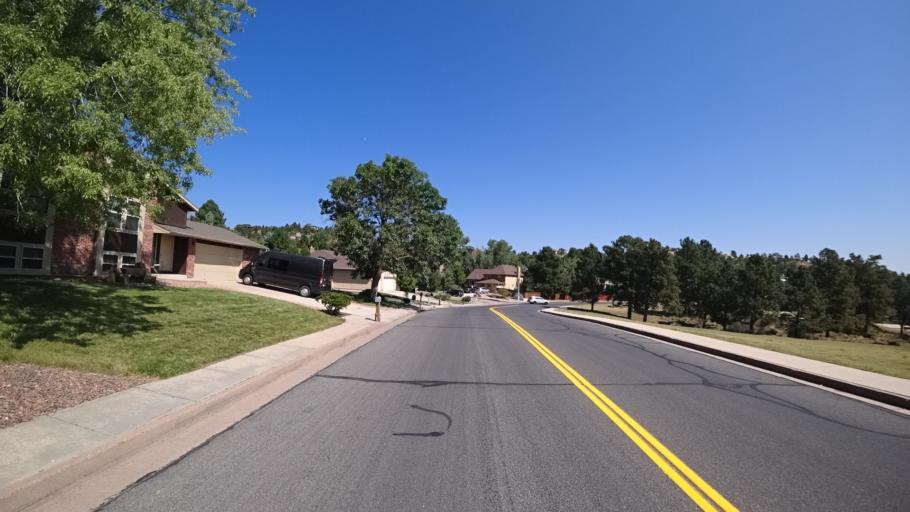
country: US
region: Colorado
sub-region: El Paso County
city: Air Force Academy
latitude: 38.9309
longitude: -104.8457
